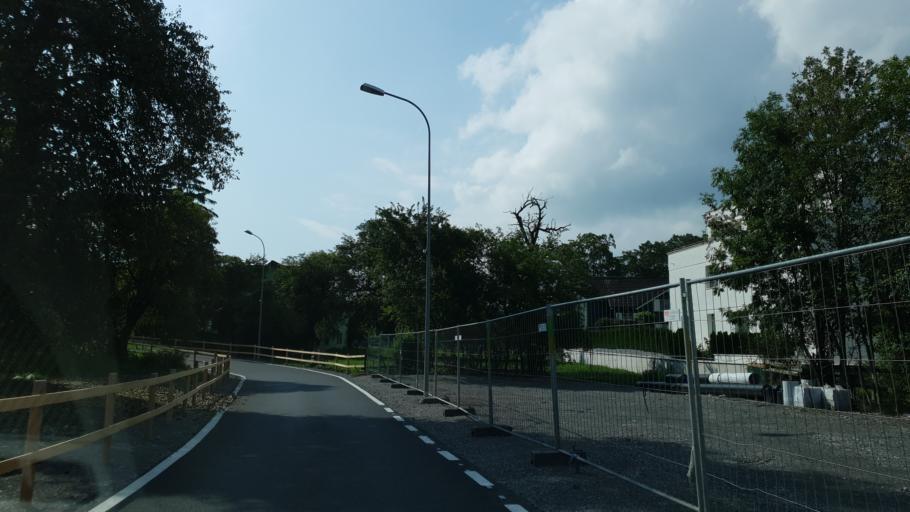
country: LI
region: Schaan
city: Schaan
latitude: 47.1636
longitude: 9.5077
